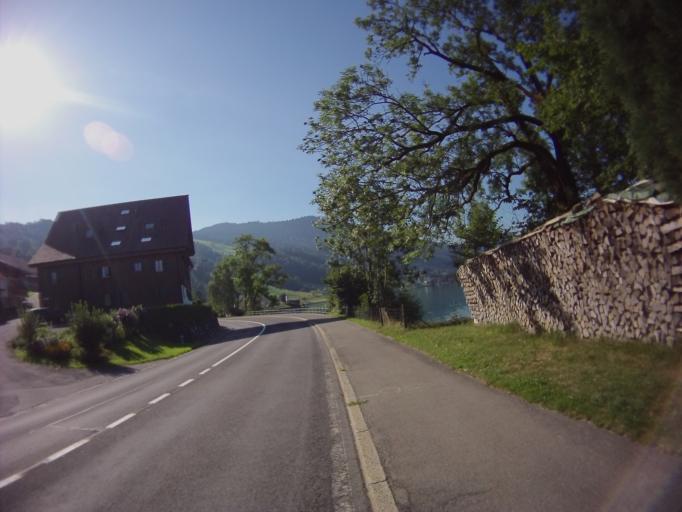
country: CH
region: Schwyz
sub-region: Bezirk Schwyz
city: Sattel
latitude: 47.1191
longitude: 8.6379
